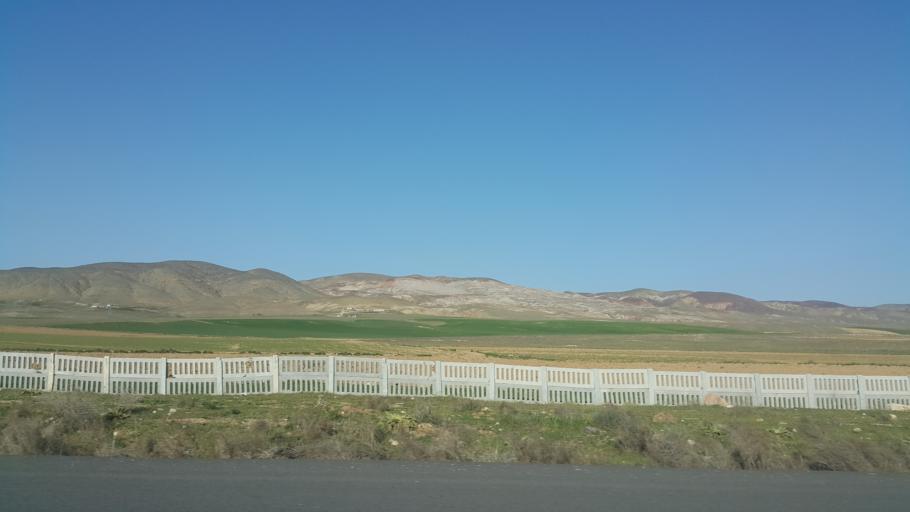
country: TR
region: Ankara
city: Sereflikochisar
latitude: 38.7289
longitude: 33.6703
